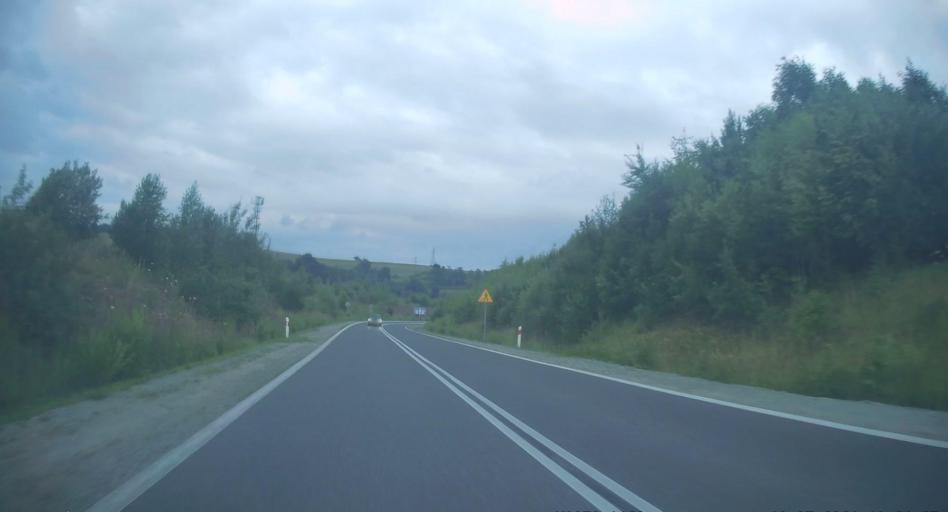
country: PL
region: Lower Silesian Voivodeship
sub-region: Powiat klodzki
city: Nowa Ruda
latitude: 50.5980
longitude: 16.5155
